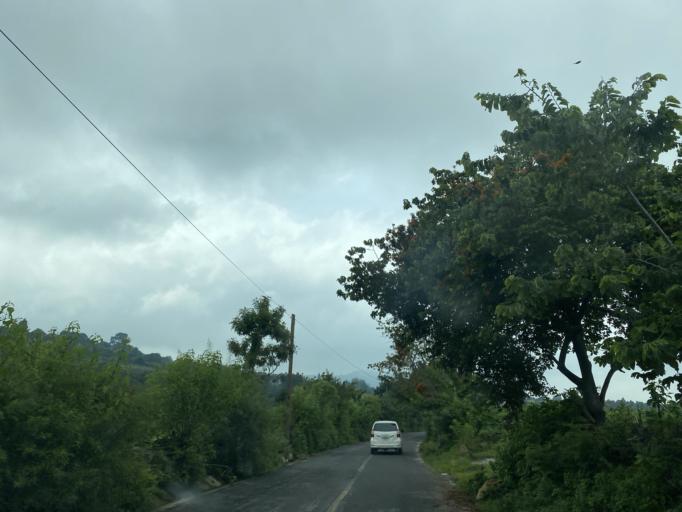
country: MX
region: Morelos
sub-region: Yecapixtla
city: Achichipico
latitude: 18.9558
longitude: -98.8259
